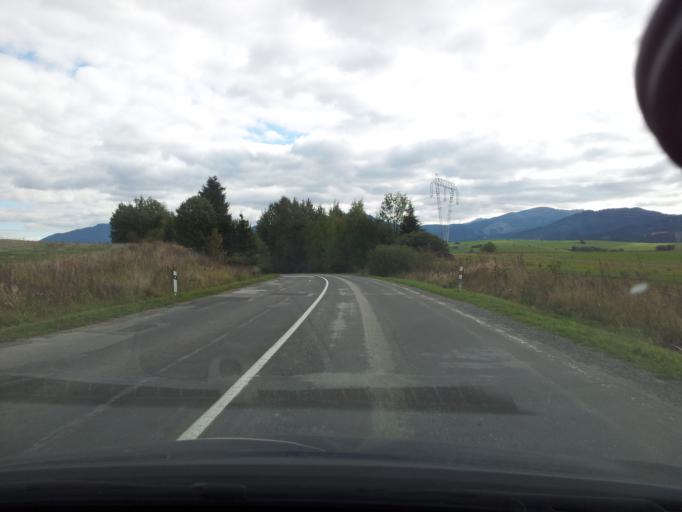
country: SK
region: Zilinsky
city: Ruzomberok
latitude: 49.0605
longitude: 19.4458
